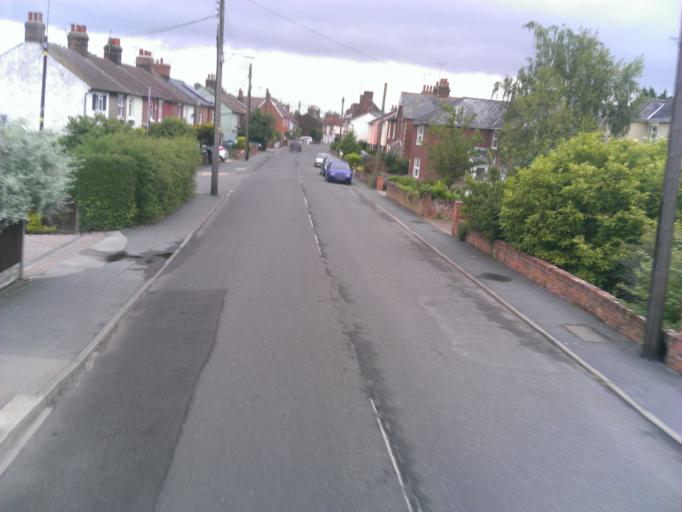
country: GB
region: England
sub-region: Essex
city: Wivenhoe
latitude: 51.8651
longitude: 0.9611
